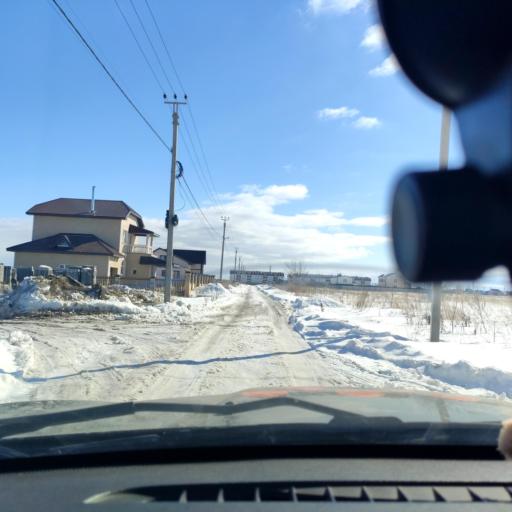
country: RU
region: Samara
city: Podstepki
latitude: 53.5243
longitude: 49.1793
